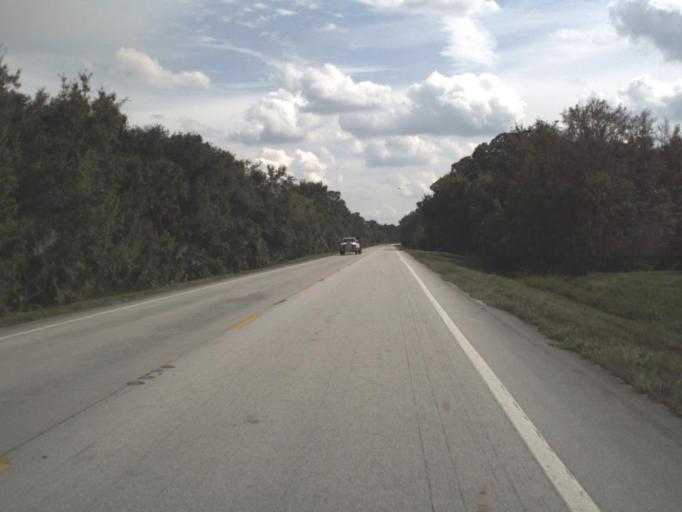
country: US
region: Florida
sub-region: Indian River County
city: Fellsmere
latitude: 27.5861
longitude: -80.8391
